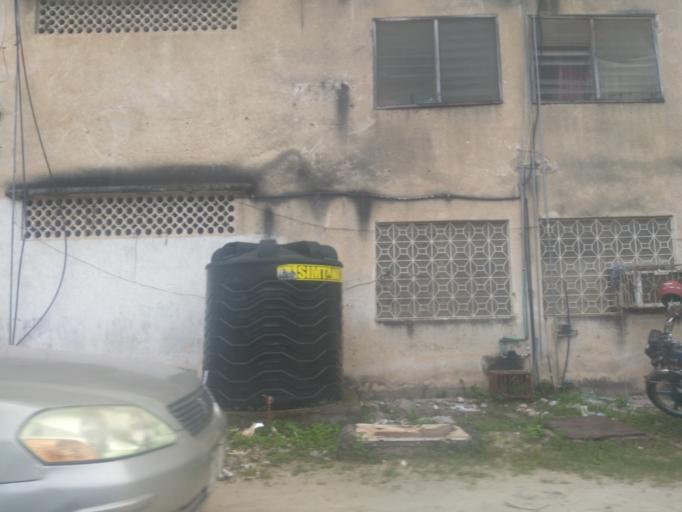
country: TZ
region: Zanzibar Urban/West
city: Zanzibar
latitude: -6.1643
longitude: 39.1986
